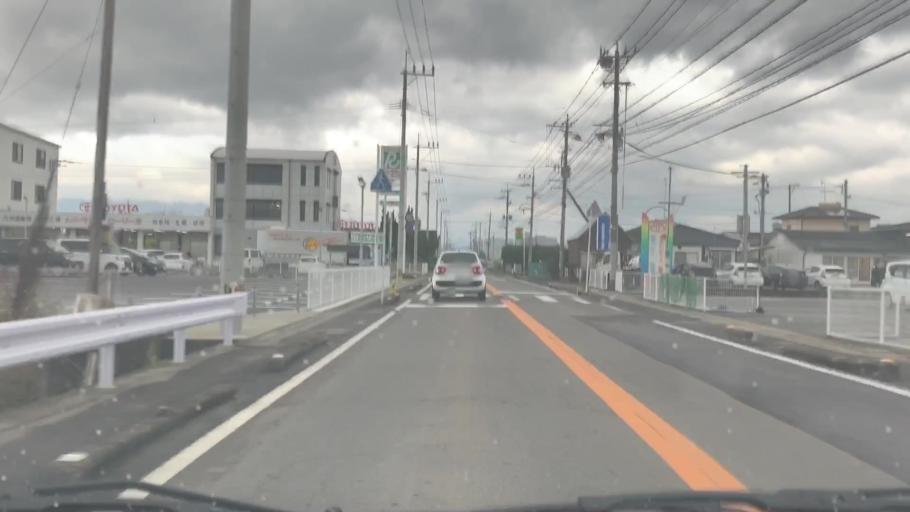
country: JP
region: Saga Prefecture
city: Saga-shi
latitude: 33.2478
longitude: 130.2655
